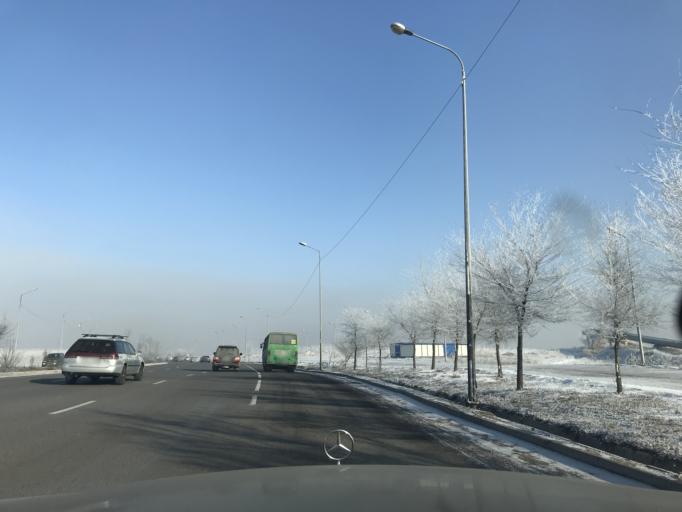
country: KZ
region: Almaty Oblysy
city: Burunday
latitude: 43.2987
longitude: 76.8347
